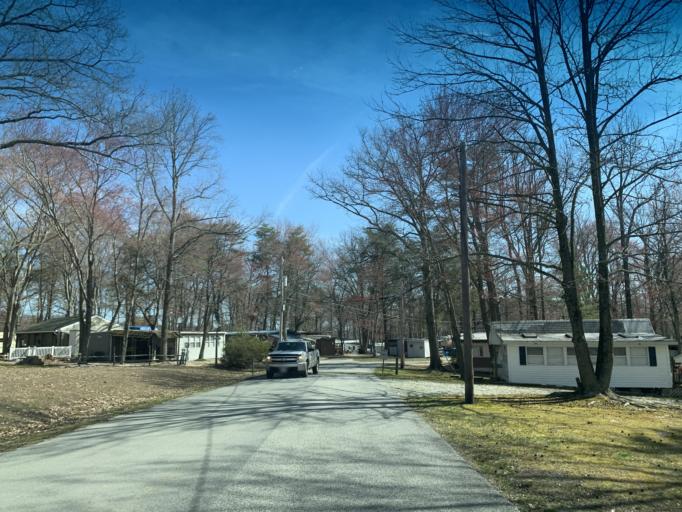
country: US
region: Maryland
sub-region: Cecil County
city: Charlestown
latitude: 39.5528
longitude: -76.0101
